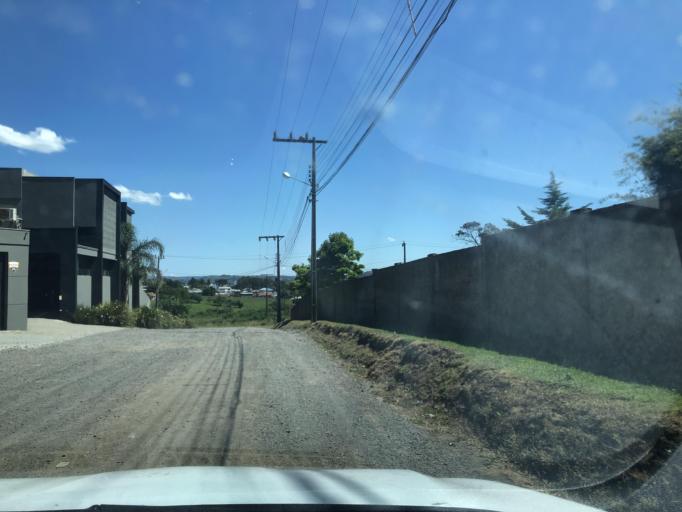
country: BR
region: Santa Catarina
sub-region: Lages
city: Lages
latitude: -27.7801
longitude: -50.3103
